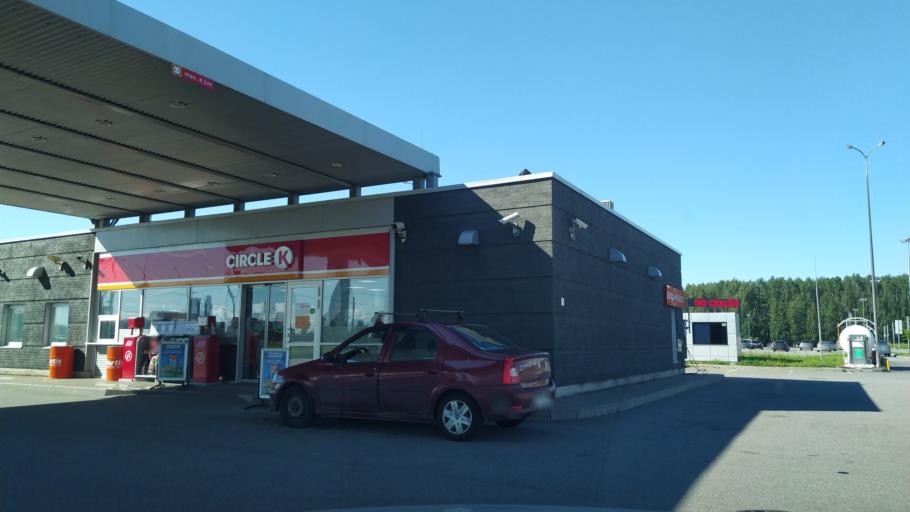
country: RU
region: St.-Petersburg
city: Krasnogvargeisky
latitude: 59.9887
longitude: 30.4667
